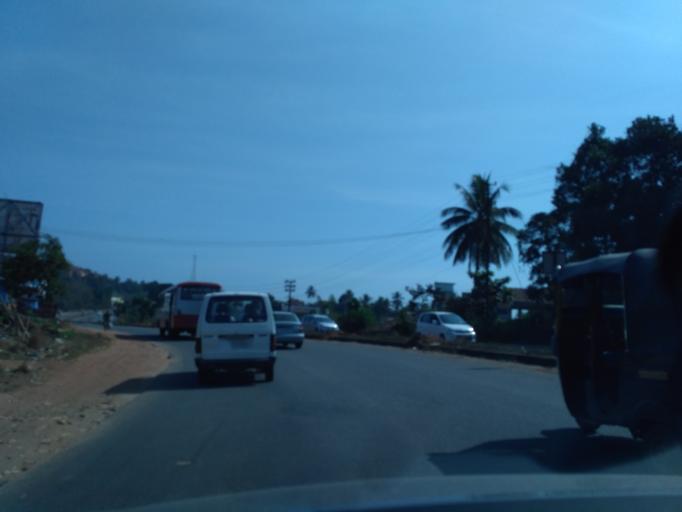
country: IN
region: Karnataka
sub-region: Dakshina Kannada
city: Bantval
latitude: 12.8760
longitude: 75.0115
